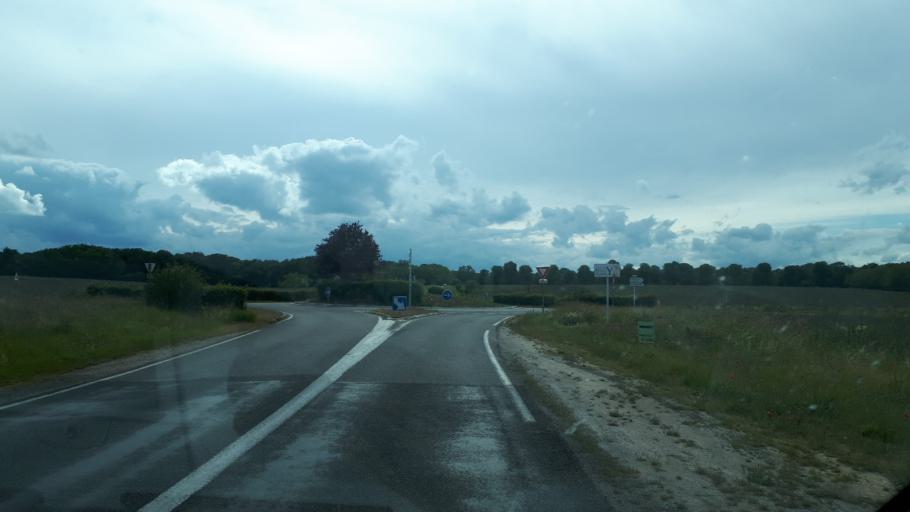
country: FR
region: Centre
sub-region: Departement du Cher
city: Mehun-sur-Yevre
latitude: 47.0780
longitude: 2.1814
